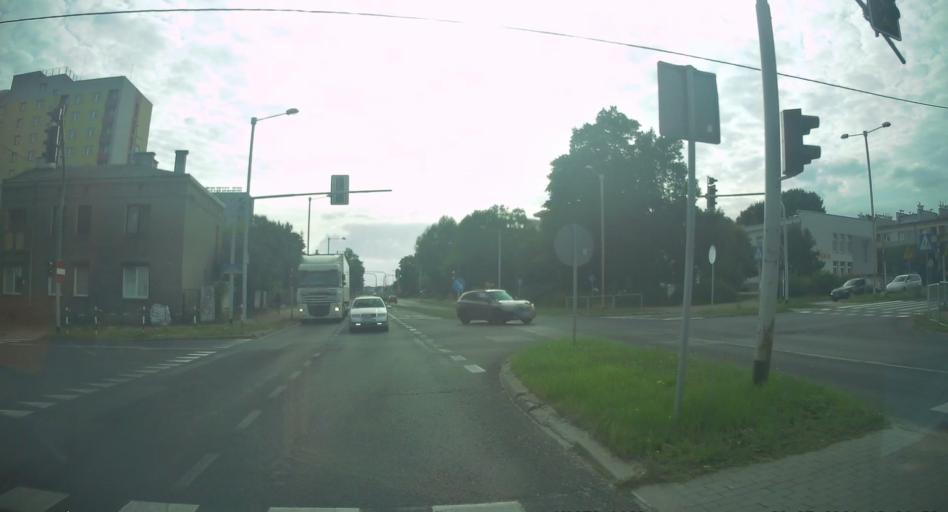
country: PL
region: Silesian Voivodeship
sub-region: Czestochowa
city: Czestochowa
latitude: 50.8251
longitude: 19.1119
